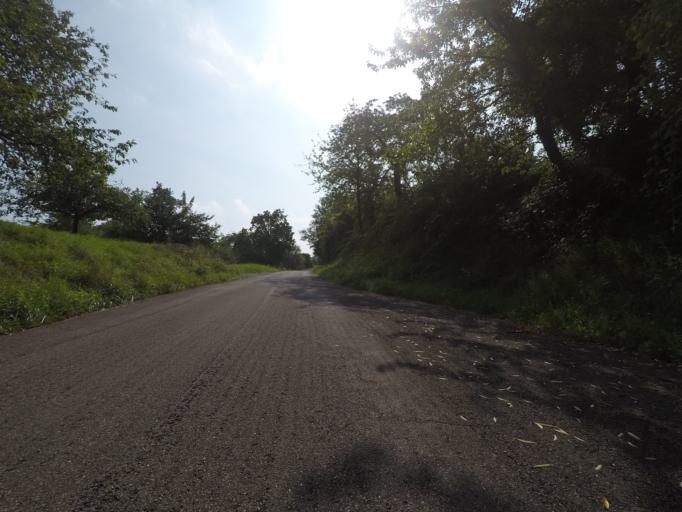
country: DE
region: Baden-Wuerttemberg
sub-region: Regierungsbezirk Stuttgart
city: Weinstadt-Endersbach
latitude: 48.8048
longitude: 9.4030
